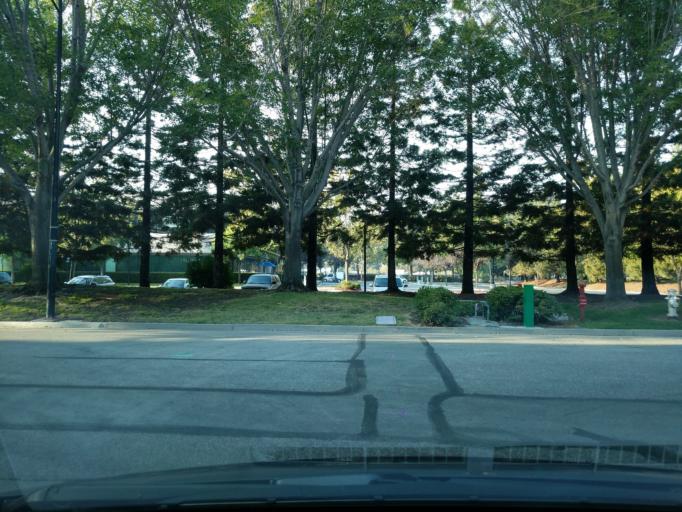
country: US
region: California
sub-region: Santa Clara County
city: Mountain View
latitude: 37.4167
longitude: -122.0836
